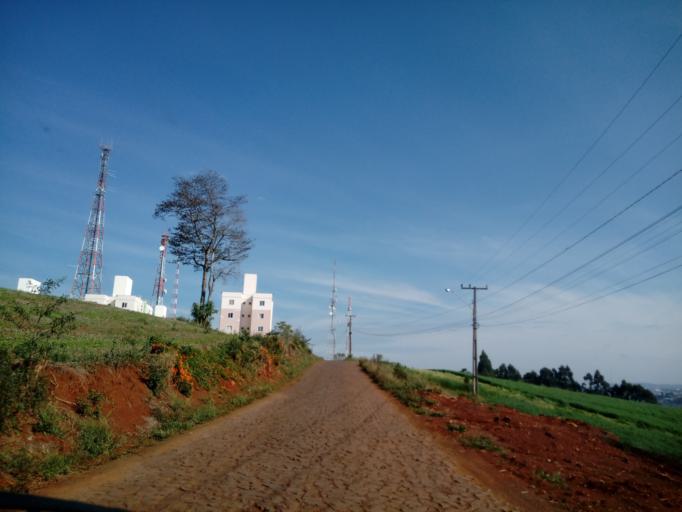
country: BR
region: Santa Catarina
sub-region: Chapeco
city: Chapeco
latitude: -27.1069
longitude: -52.5781
